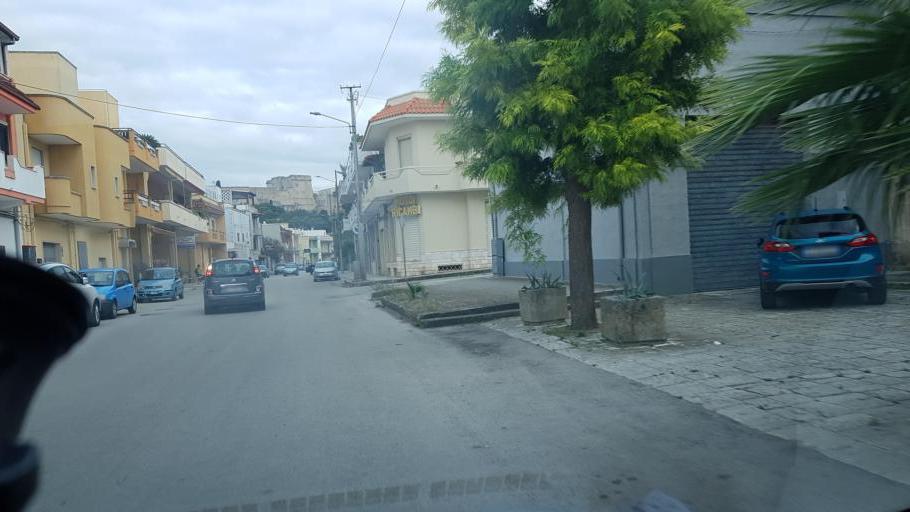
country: IT
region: Apulia
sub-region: Provincia di Brindisi
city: Oria
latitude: 40.5010
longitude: 17.6363
